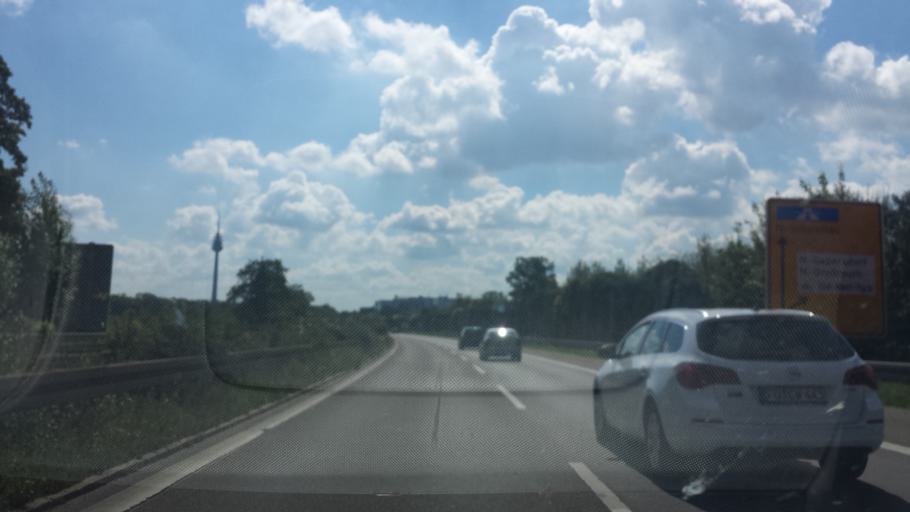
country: DE
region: Bavaria
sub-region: Regierungsbezirk Mittelfranken
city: Grossreuth bei Schweinau
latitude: 49.4342
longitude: 11.0087
